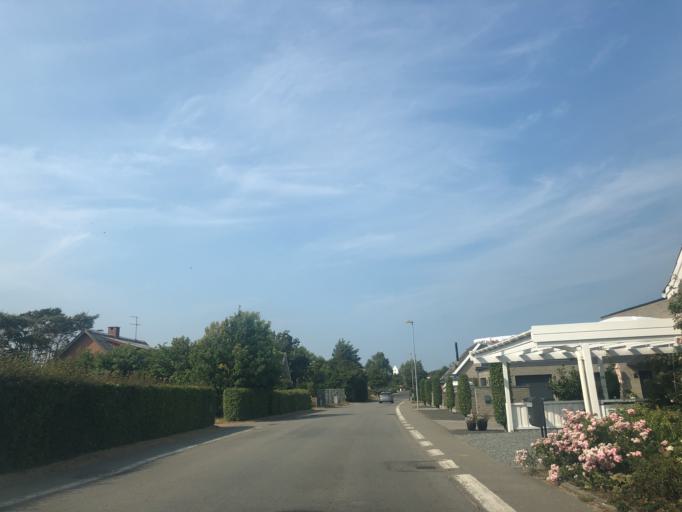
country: DK
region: North Denmark
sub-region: Morso Kommune
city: Nykobing Mors
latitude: 56.8064
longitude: 9.0203
